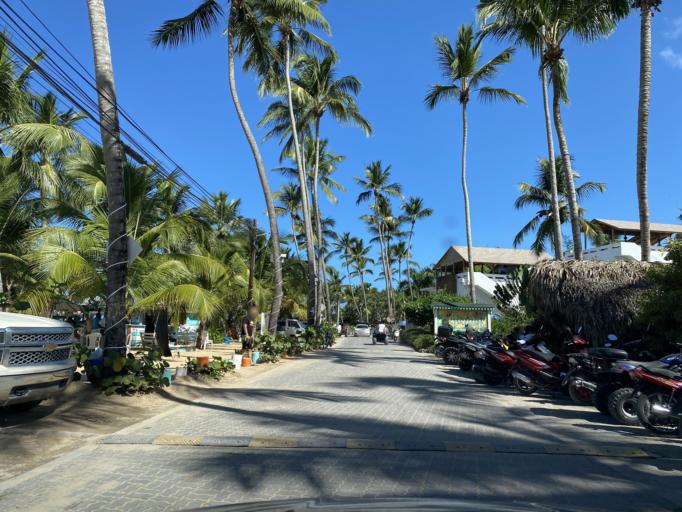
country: DO
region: Samana
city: Las Terrenas
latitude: 19.3254
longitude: -69.5516
